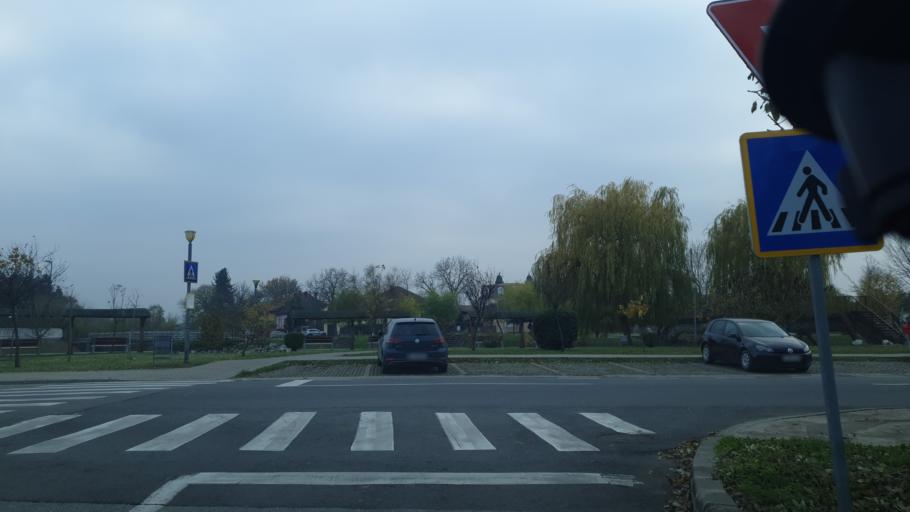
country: RO
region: Timis
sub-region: Comuna Ghiroda
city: Ghiroda
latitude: 45.7608
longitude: 21.2638
